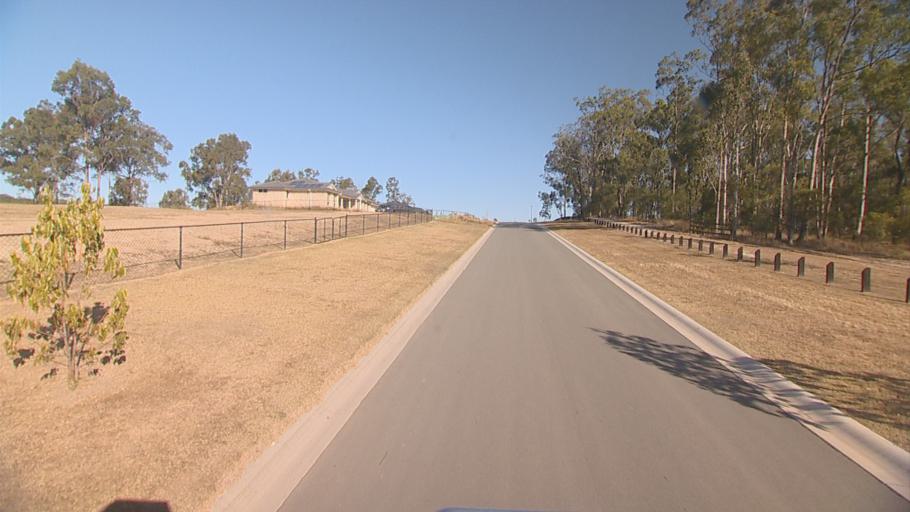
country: AU
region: Queensland
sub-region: Logan
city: Cedar Vale
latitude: -27.8643
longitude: 153.0538
